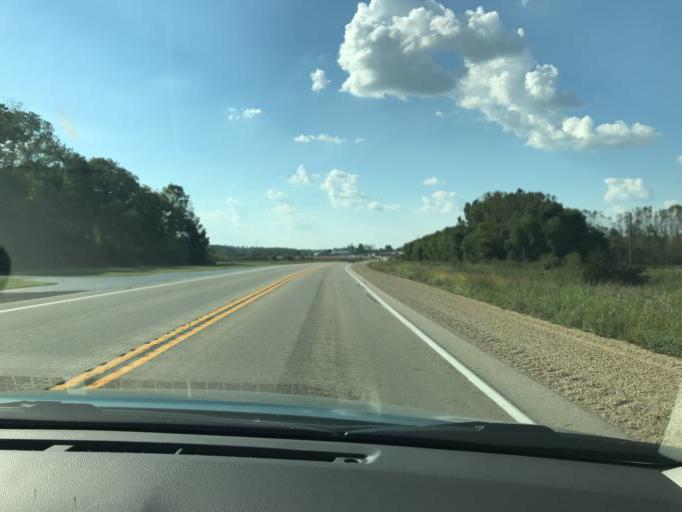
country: US
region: Wisconsin
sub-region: Green County
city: Brodhead
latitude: 42.5894
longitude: -89.4886
